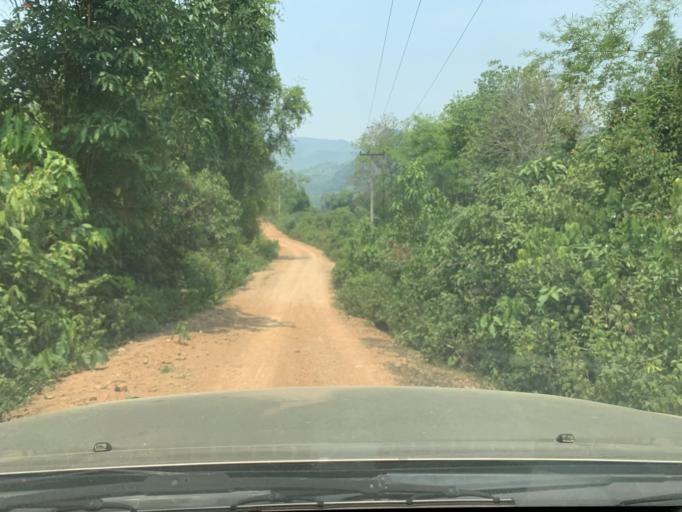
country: LA
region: Louangphabang
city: Louangphabang
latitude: 19.9669
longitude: 102.1271
